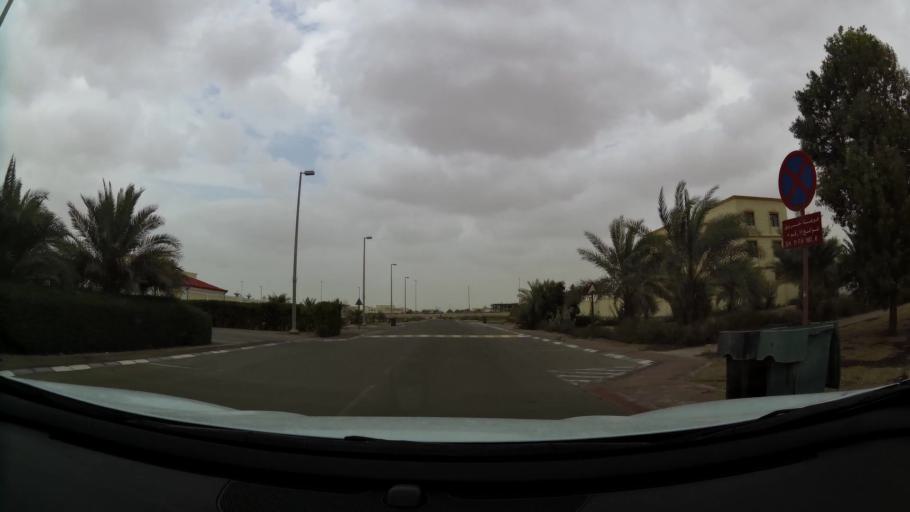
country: AE
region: Abu Dhabi
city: Abu Dhabi
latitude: 24.3324
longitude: 54.6438
